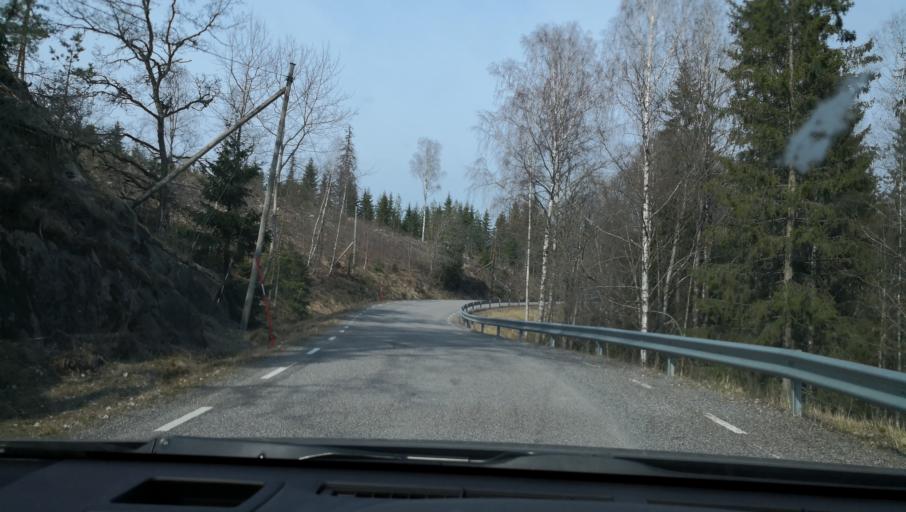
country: SE
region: OErebro
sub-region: Lindesbergs Kommun
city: Frovi
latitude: 59.3862
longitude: 15.3877
